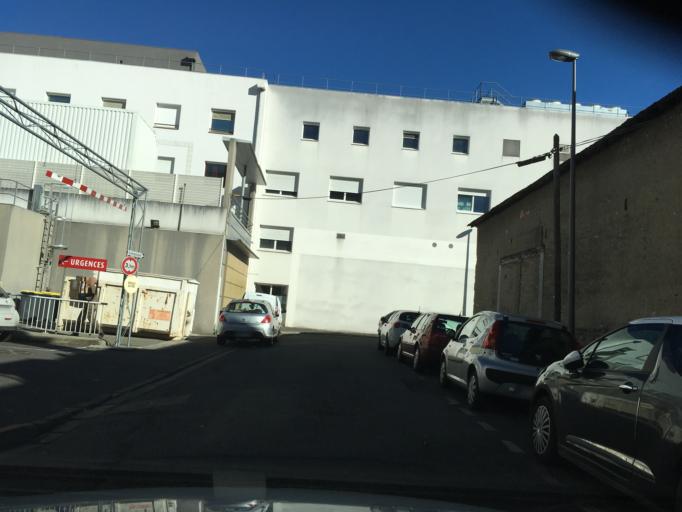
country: FR
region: Aquitaine
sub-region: Departement des Pyrenees-Atlantiques
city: Pau
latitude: 43.3038
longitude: -0.3641
